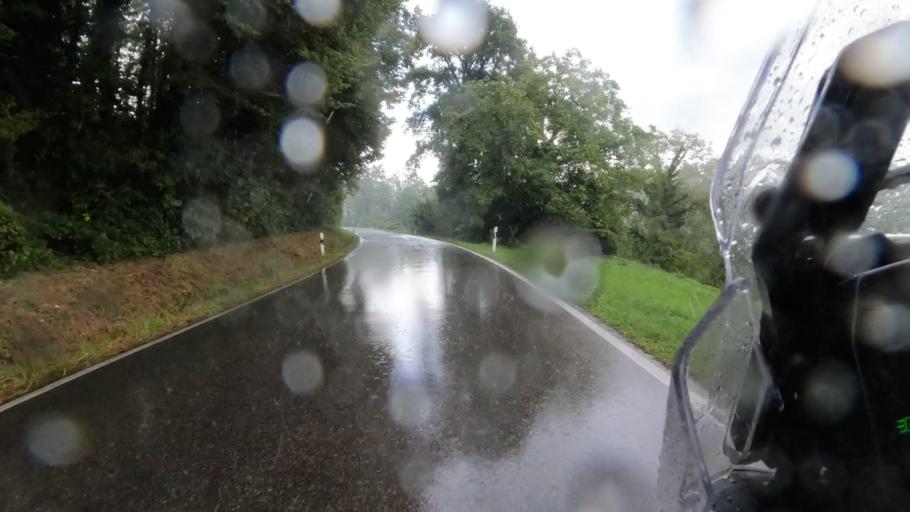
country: CH
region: Zurich
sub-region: Bezirk Andelfingen
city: Dachsen
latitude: 47.6458
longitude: 8.5986
